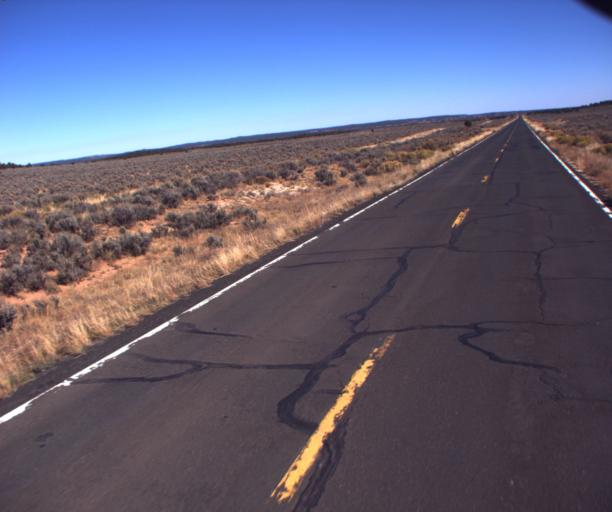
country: US
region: Arizona
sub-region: Navajo County
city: First Mesa
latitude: 35.7578
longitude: -110.0177
